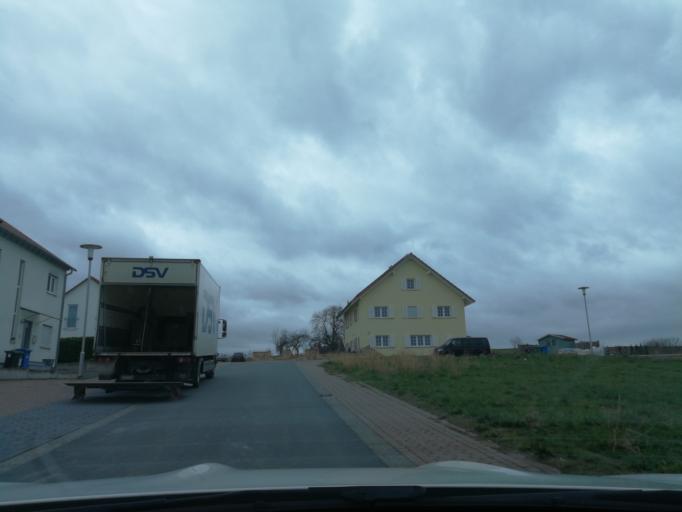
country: DE
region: Hesse
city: Reinheim
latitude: 49.8470
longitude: 8.8309
